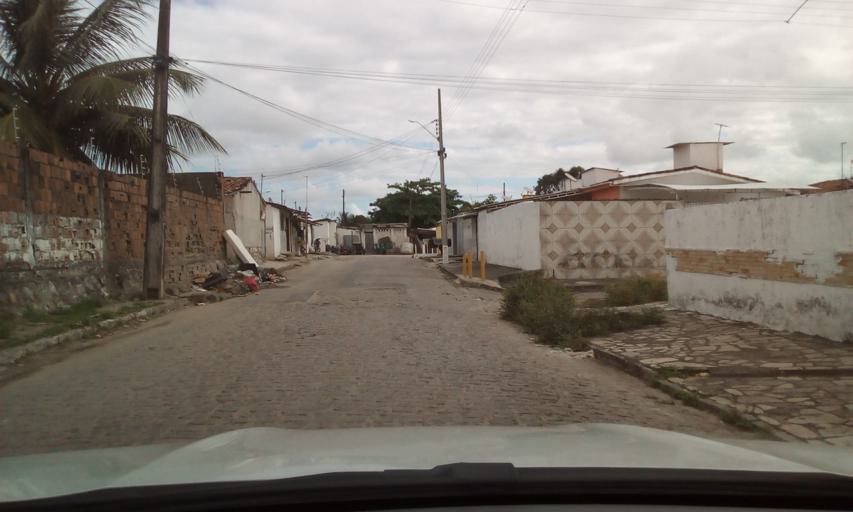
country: BR
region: Paraiba
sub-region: Joao Pessoa
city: Joao Pessoa
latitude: -7.1822
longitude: -34.8772
